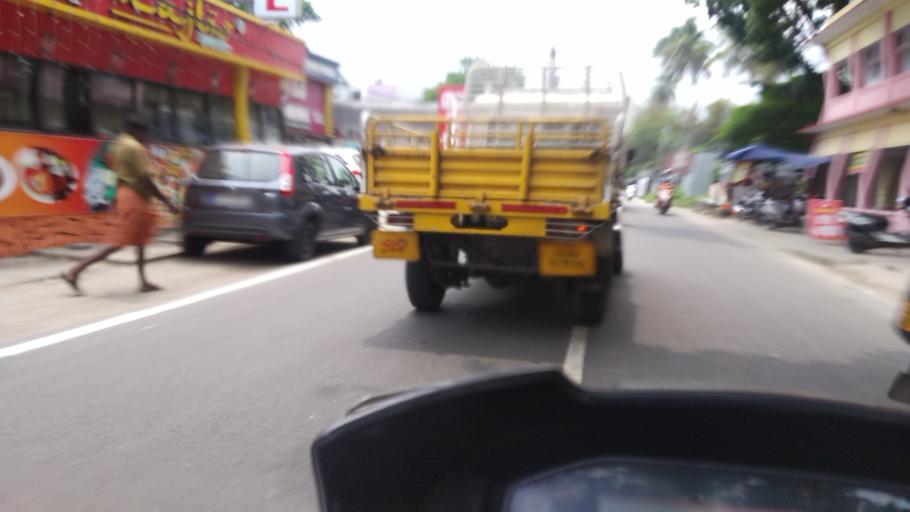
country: IN
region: Kerala
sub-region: Thrissur District
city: Kodungallur
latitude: 10.1394
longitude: 76.1956
